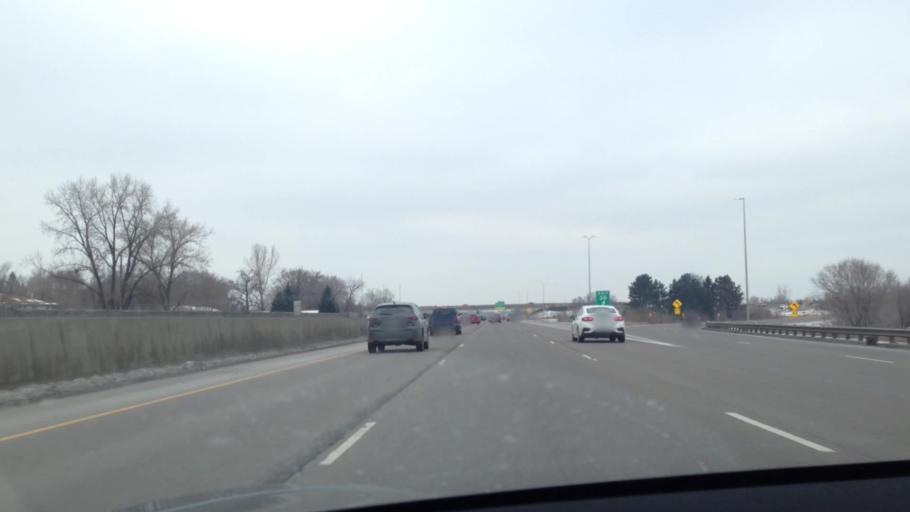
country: US
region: Minnesota
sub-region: Ramsey County
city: Mounds View
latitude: 45.1106
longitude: -93.1883
